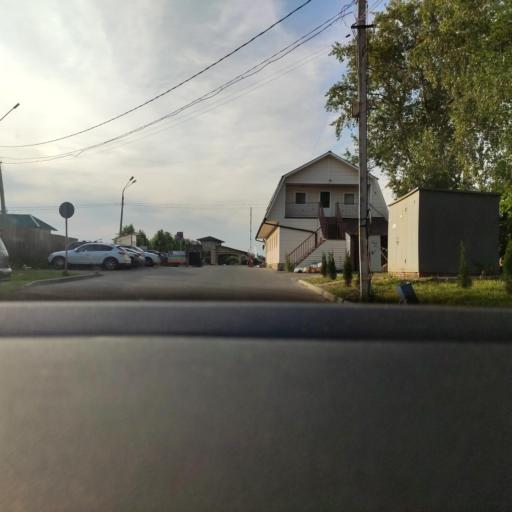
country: RU
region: Moscow
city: Lianozovo
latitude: 55.9245
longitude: 37.6041
